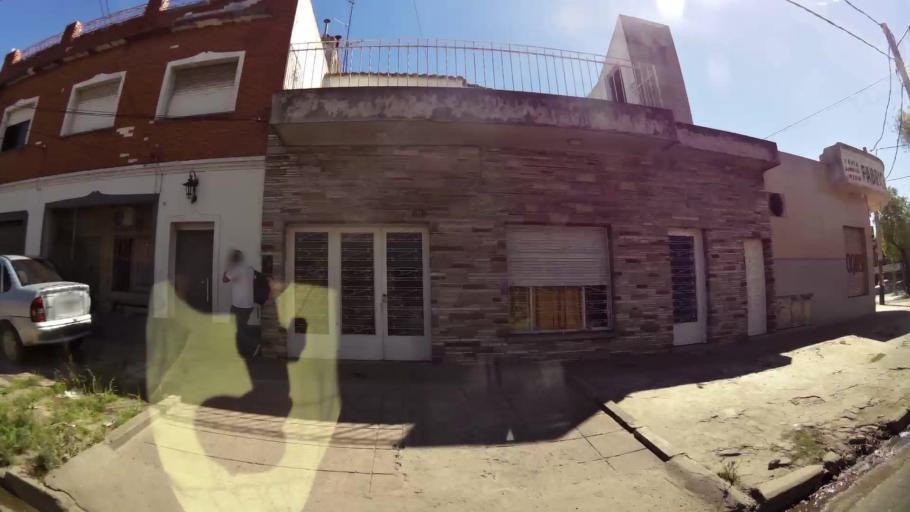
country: AR
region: Buenos Aires
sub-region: Partido de Almirante Brown
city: Adrogue
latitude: -34.7622
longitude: -58.3623
